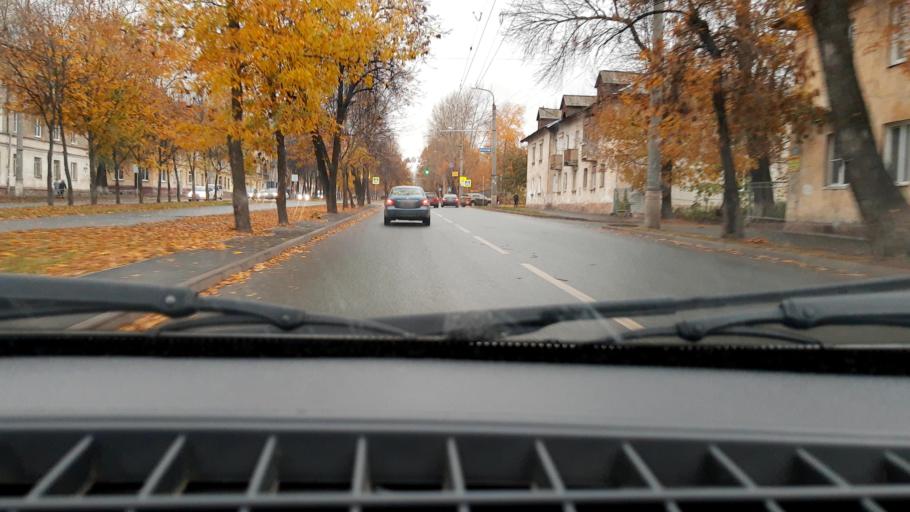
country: RU
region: Bashkortostan
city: Ufa
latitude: 54.8205
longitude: 56.0997
